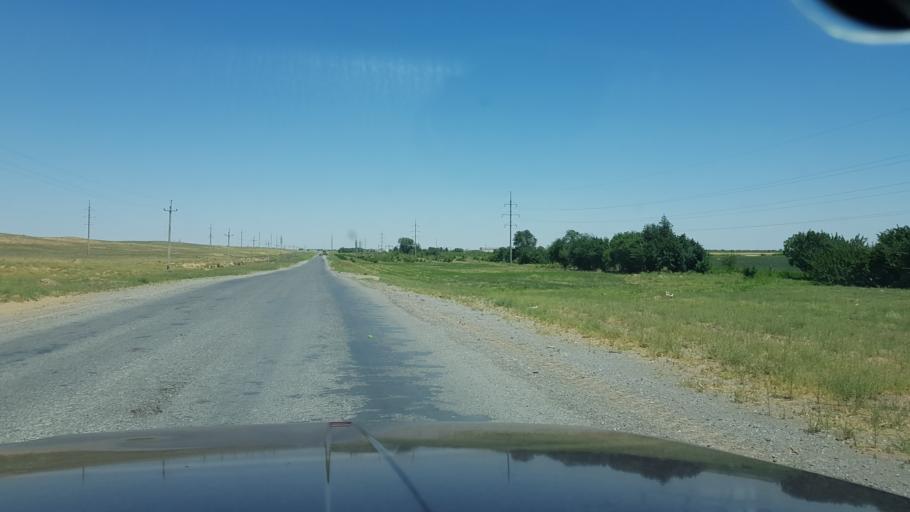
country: TM
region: Ahal
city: Annau
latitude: 37.8763
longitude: 58.7240
